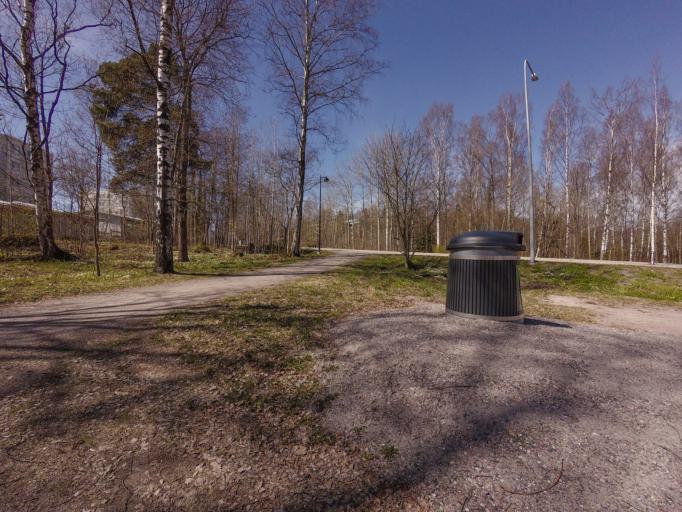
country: FI
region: Uusimaa
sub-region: Helsinki
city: Vantaa
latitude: 60.2018
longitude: 25.0684
